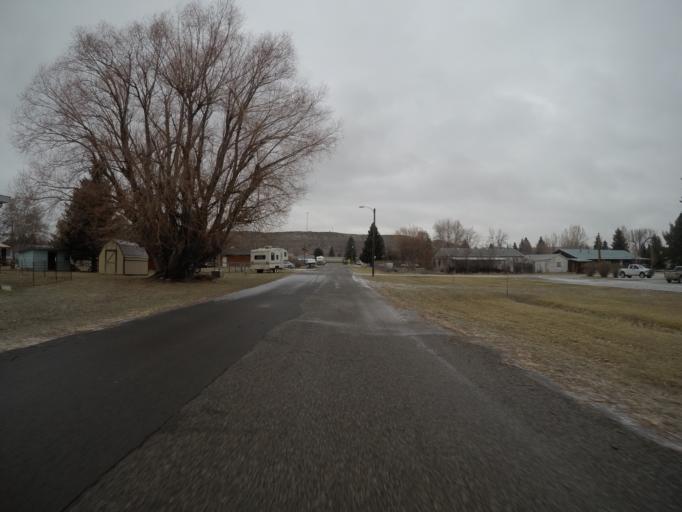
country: US
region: Montana
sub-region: Stillwater County
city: Absarokee
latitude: 45.5158
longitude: -109.4422
